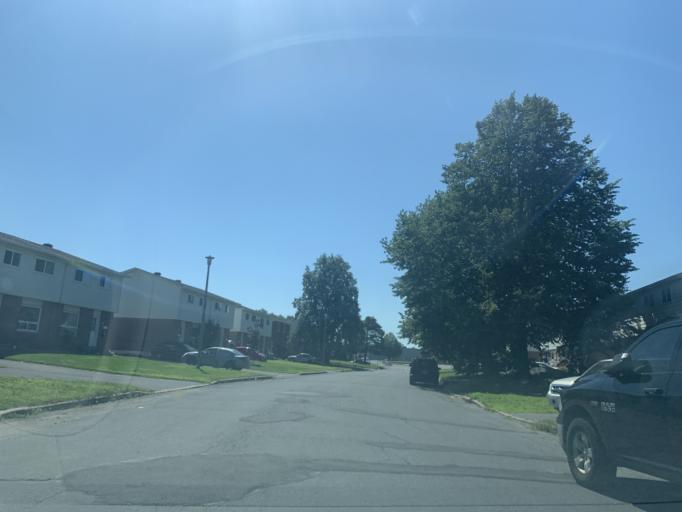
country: CA
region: Ontario
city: Hawkesbury
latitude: 45.6026
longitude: -74.6161
